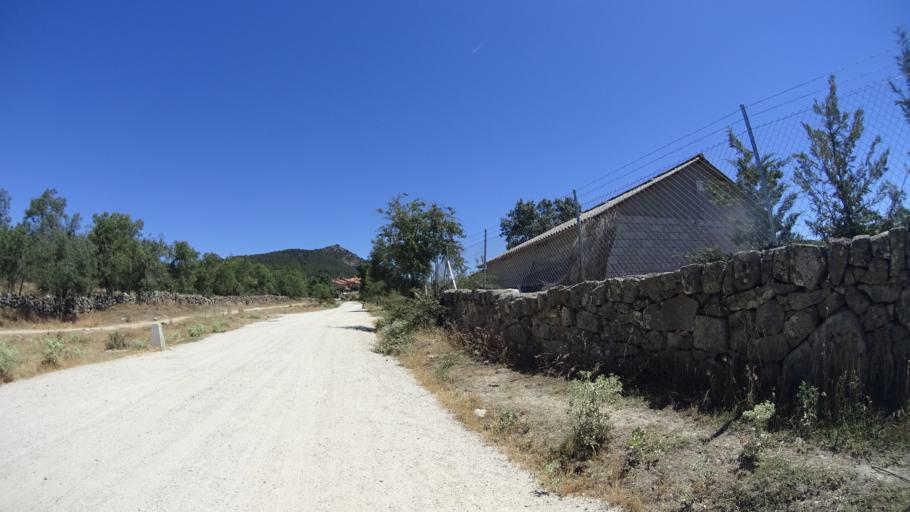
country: ES
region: Madrid
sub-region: Provincia de Madrid
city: Collado Mediano
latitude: 40.6867
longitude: -4.0337
